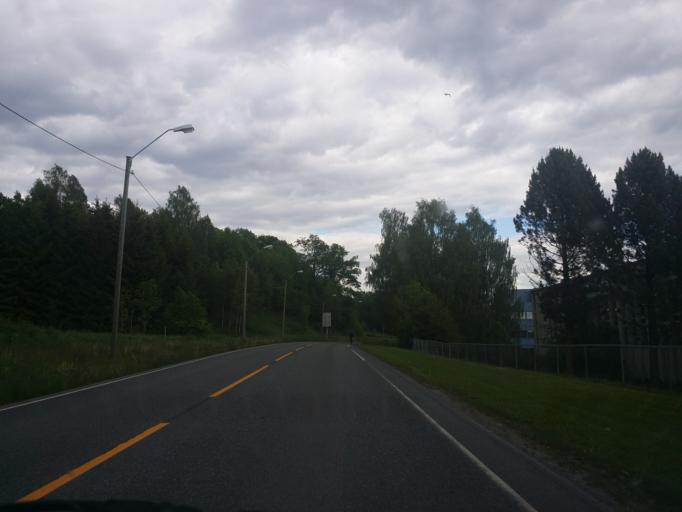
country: NO
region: Akershus
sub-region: Baerum
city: Lysaker
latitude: 59.9477
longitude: 10.5984
